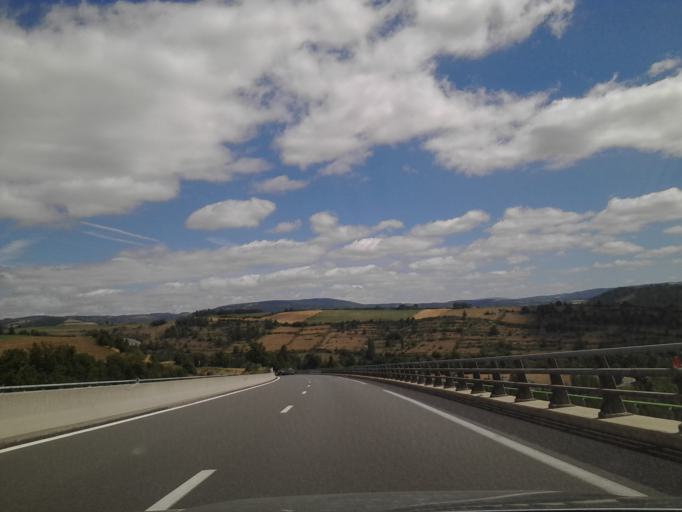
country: FR
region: Languedoc-Roussillon
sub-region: Departement de la Lozere
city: Chirac
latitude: 44.5303
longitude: 3.2480
